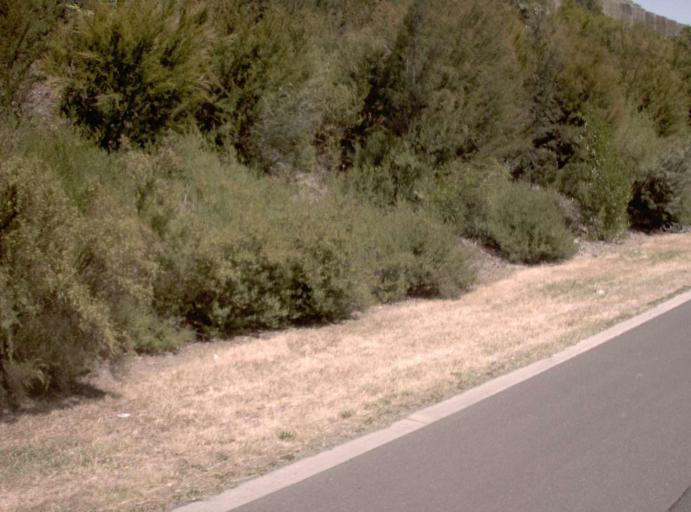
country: AU
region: Victoria
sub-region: Casey
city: Narre Warren North
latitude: -38.0046
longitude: 145.2981
